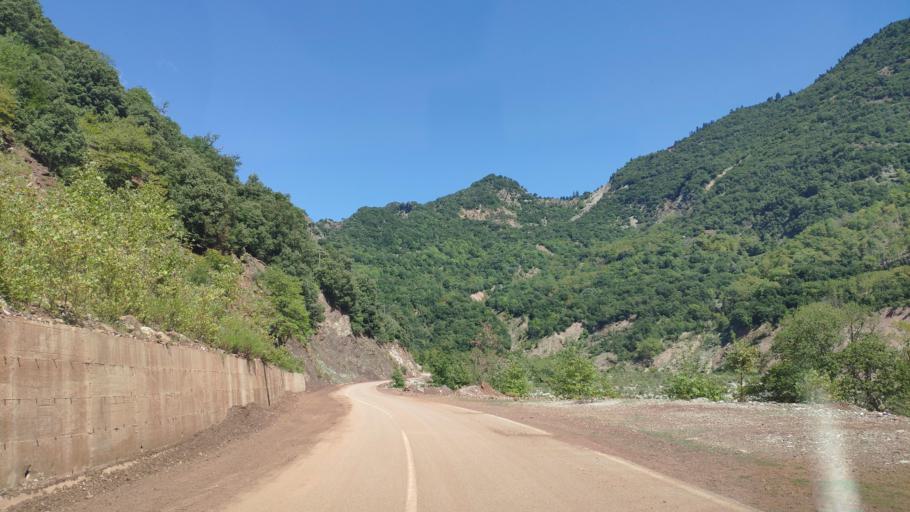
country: GR
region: Central Greece
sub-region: Nomos Evrytanias
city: Kerasochori
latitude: 39.0653
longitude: 21.6067
